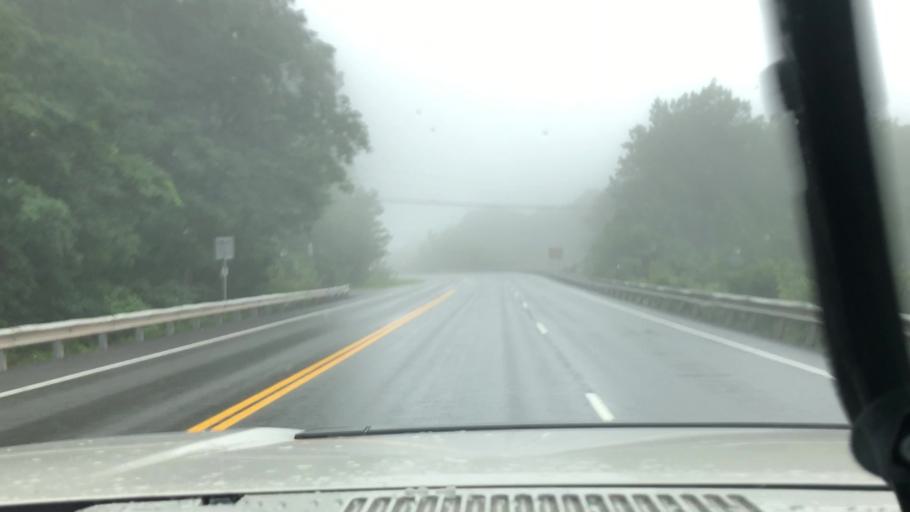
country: US
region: New York
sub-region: Greene County
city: Cairo
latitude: 42.3335
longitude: -74.1441
